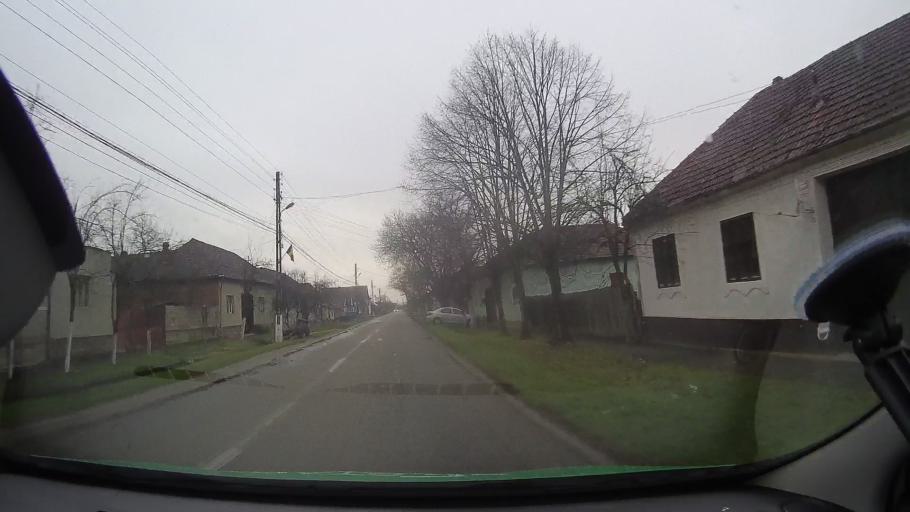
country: RO
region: Arad
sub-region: Comuna Dezna
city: Dezna
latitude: 46.4061
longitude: 22.2307
